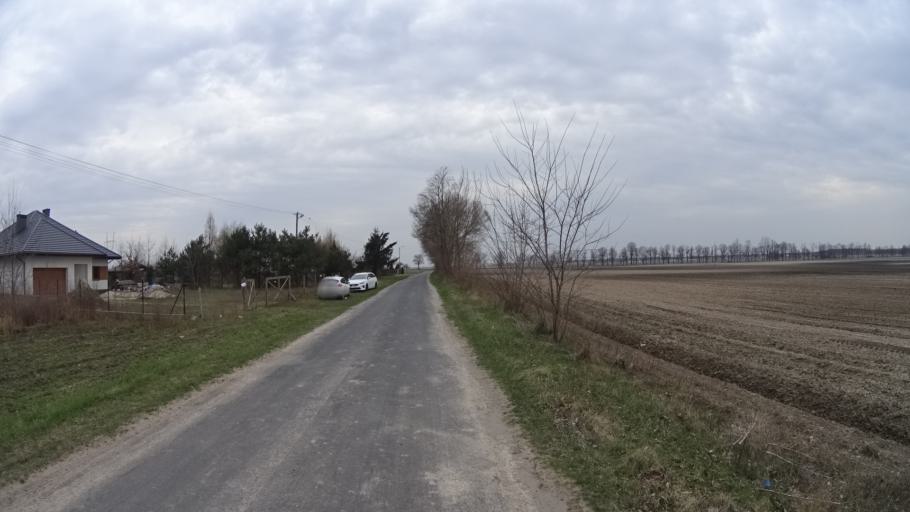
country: PL
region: Masovian Voivodeship
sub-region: Powiat warszawski zachodni
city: Blonie
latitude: 52.2478
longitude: 20.6544
